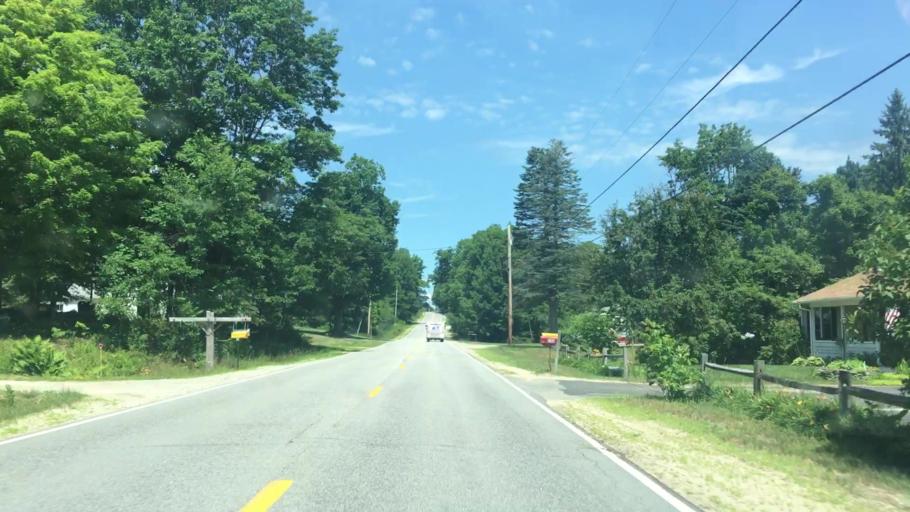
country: US
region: Maine
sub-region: Androscoggin County
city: Livermore
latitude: 44.3646
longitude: -70.2052
